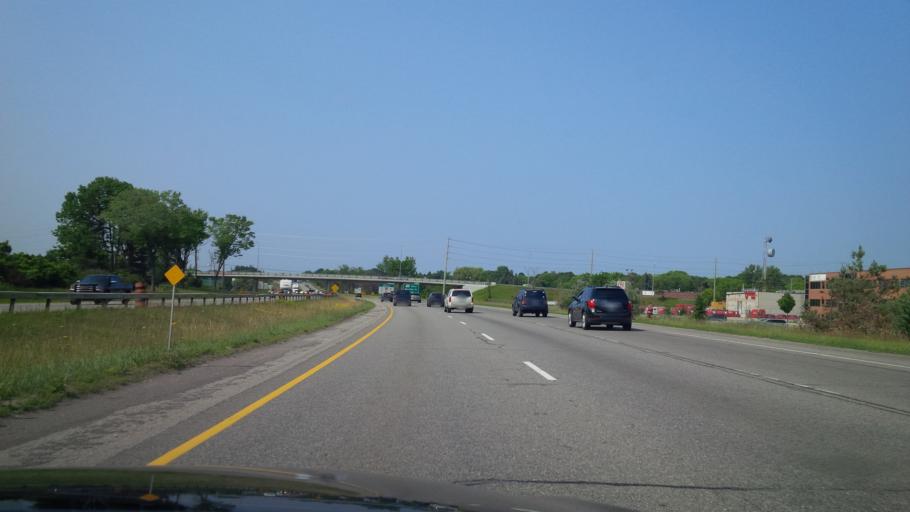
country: CA
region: Ontario
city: Barrie
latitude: 44.4107
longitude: -79.6843
